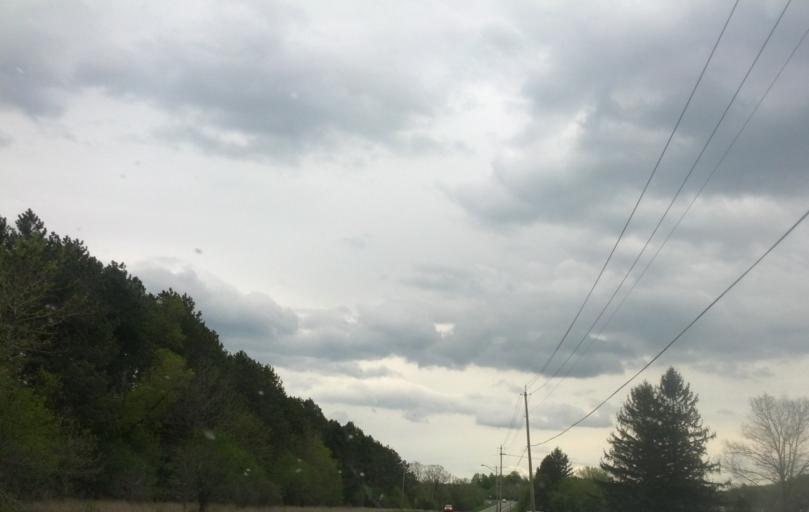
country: US
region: New York
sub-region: Onondaga County
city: Fayetteville
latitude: 42.9923
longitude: -76.0469
